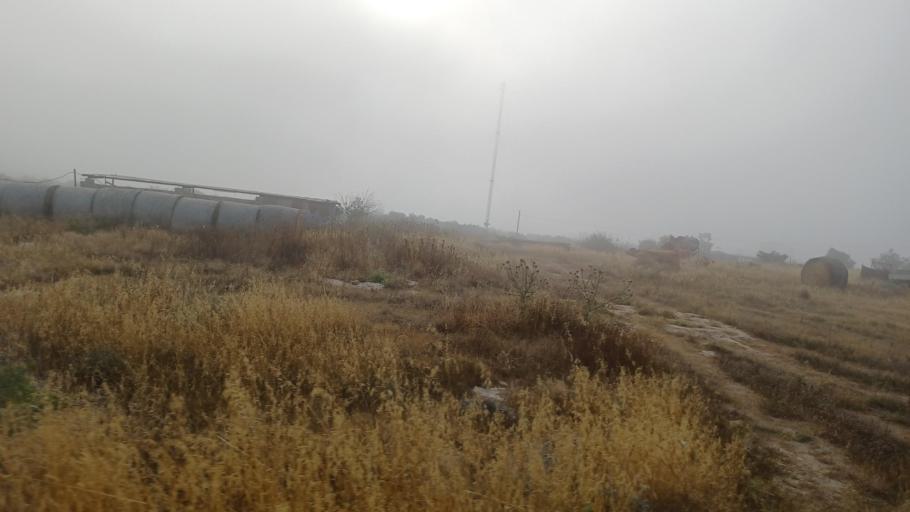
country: CY
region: Ammochostos
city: Acheritou
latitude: 35.1019
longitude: 33.8760
